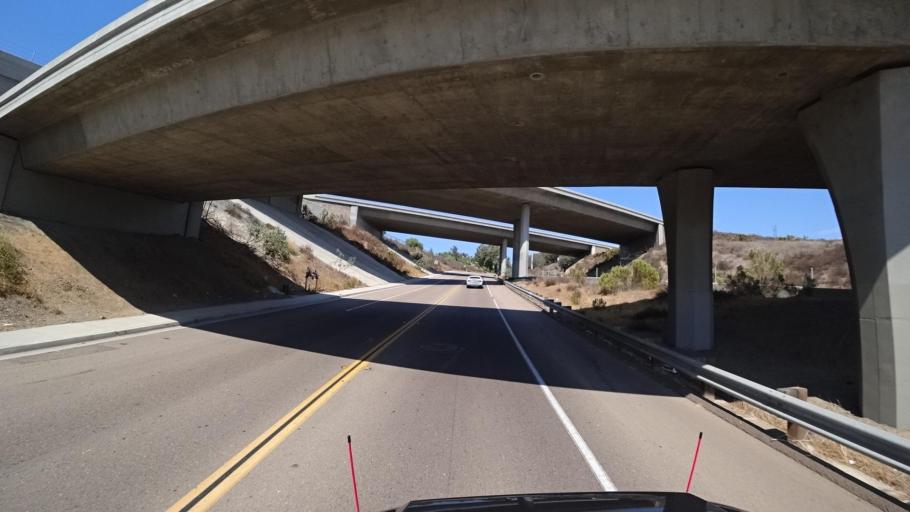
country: US
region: California
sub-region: San Diego County
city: La Presa
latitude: 32.6908
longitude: -117.0169
